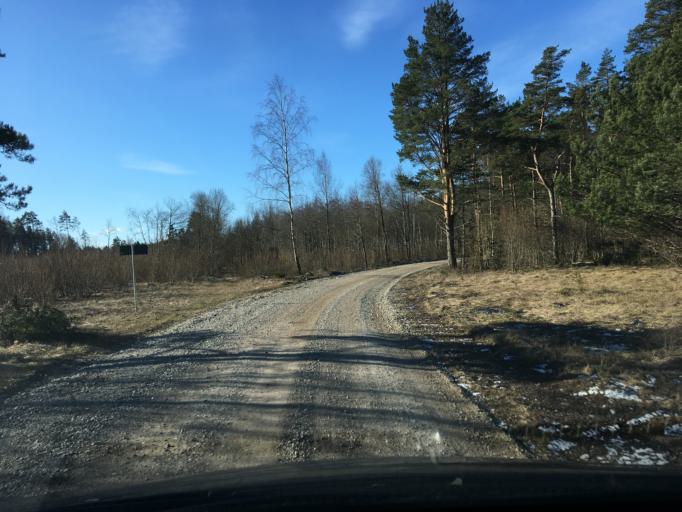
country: EE
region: Laeaene
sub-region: Lihula vald
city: Lihula
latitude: 58.5730
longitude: 23.6968
